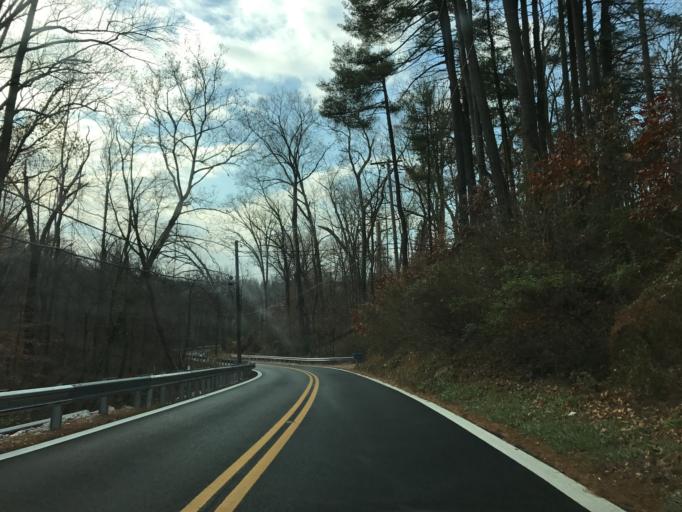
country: US
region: Maryland
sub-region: Baltimore County
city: Hunt Valley
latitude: 39.5816
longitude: -76.5985
